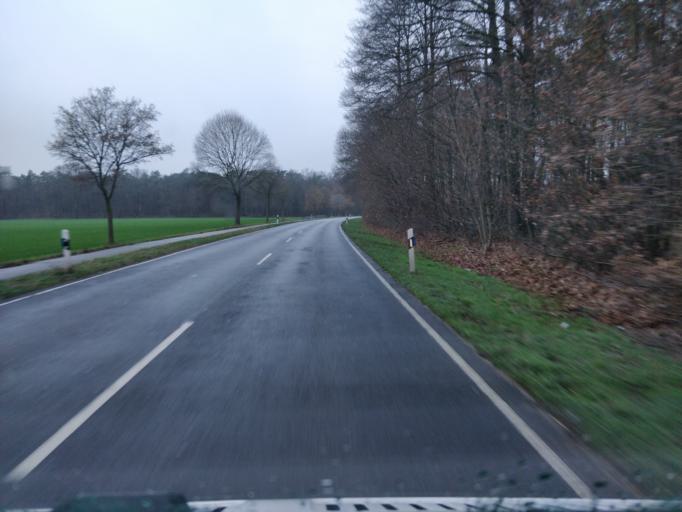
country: DE
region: North Rhine-Westphalia
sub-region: Regierungsbezirk Dusseldorf
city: Mehrhoog
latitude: 51.7433
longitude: 6.5400
